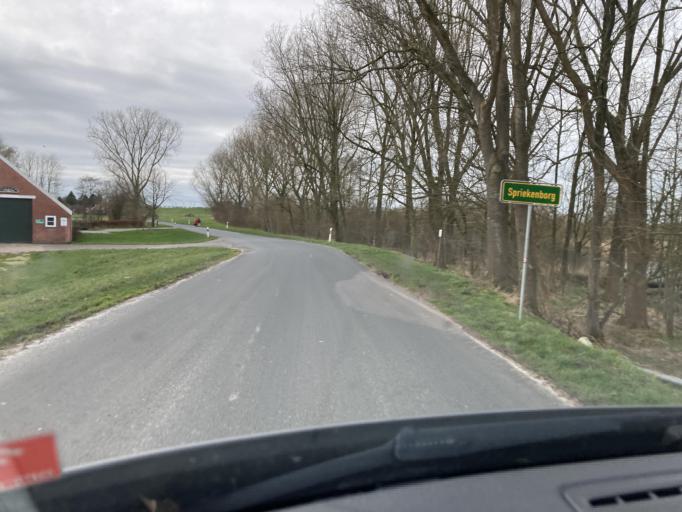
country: DE
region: Lower Saxony
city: Leer
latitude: 53.2097
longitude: 7.4745
